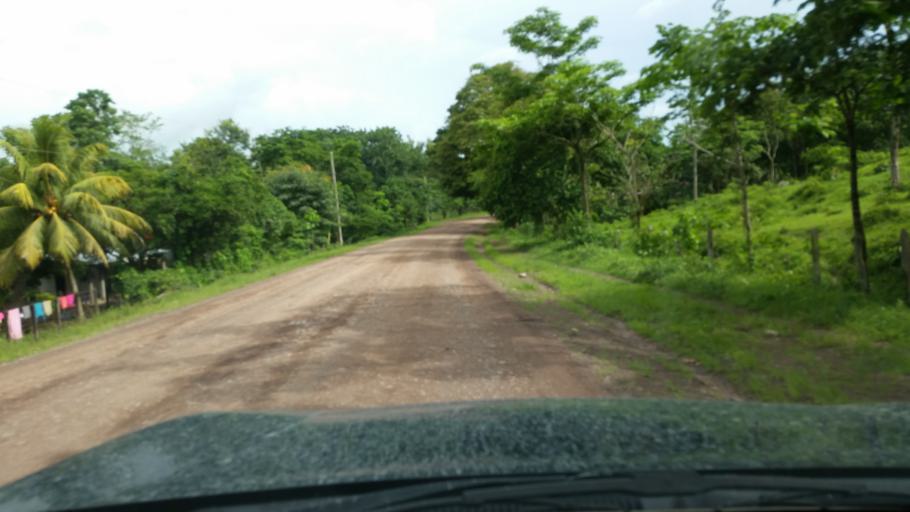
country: NI
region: Atlantico Norte (RAAN)
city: Siuna
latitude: 13.4997
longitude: -84.8430
